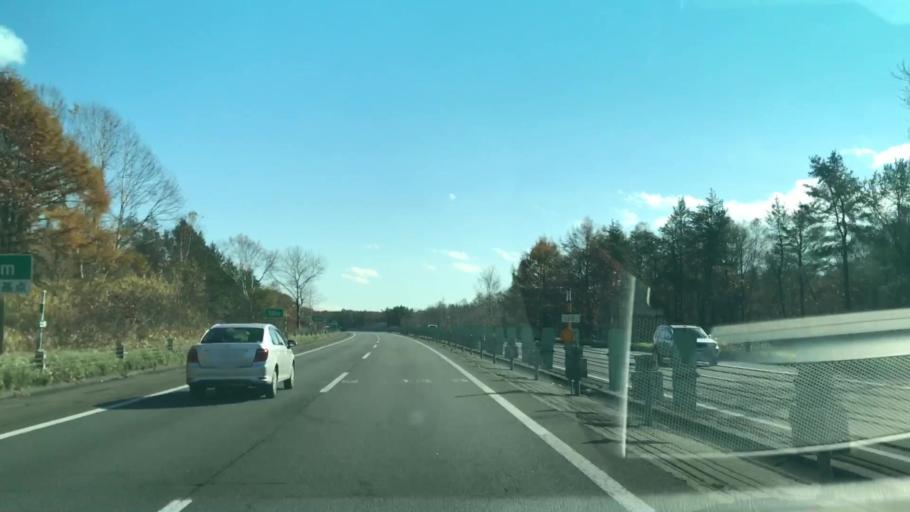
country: JP
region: Hokkaido
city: Chitose
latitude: 42.8564
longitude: 141.5629
